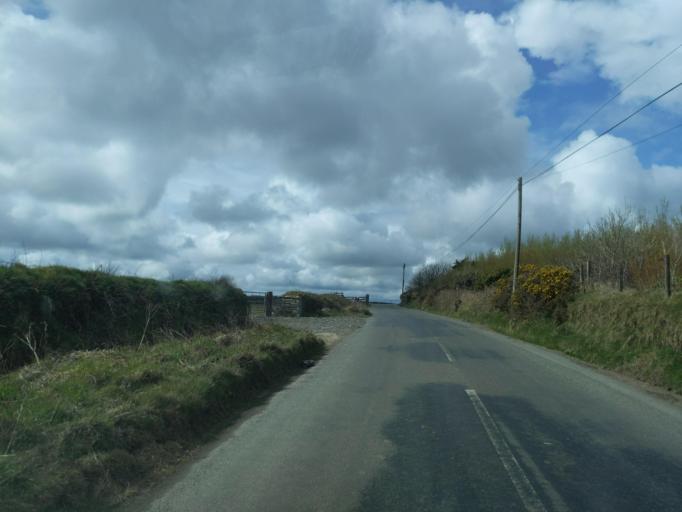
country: GB
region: England
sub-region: Cornwall
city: Camelford
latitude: 50.6274
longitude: -4.5971
